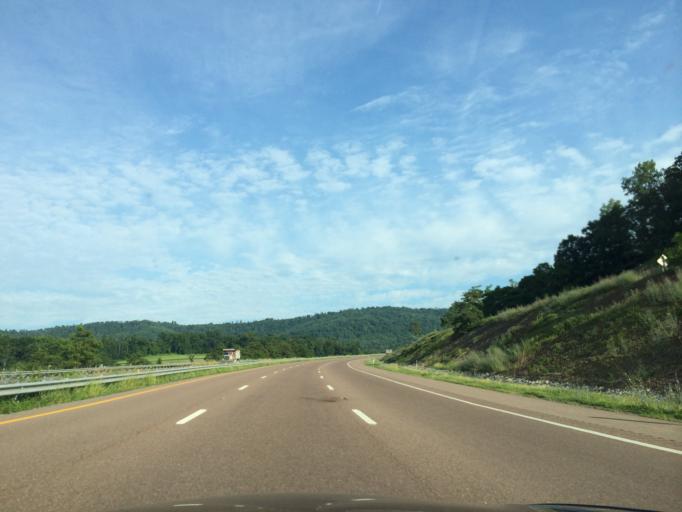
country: US
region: Maryland
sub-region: Allegany County
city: Cumberland
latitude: 39.7085
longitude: -78.5998
